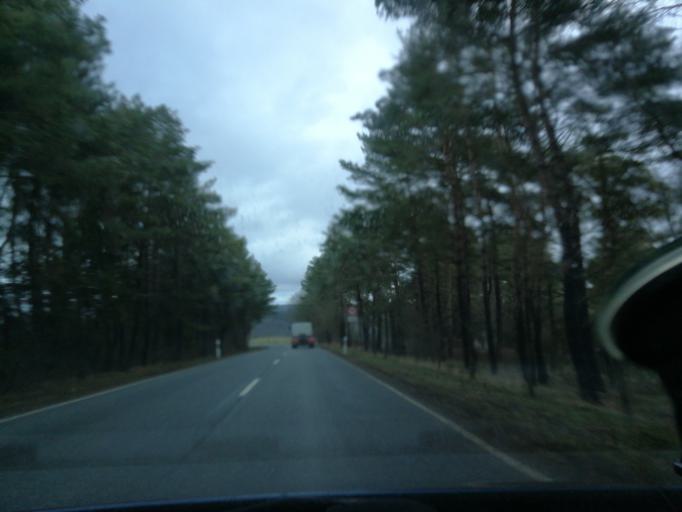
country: DE
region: Rheinland-Pfalz
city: Oberehe-Stroheich
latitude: 50.3044
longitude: 6.7664
